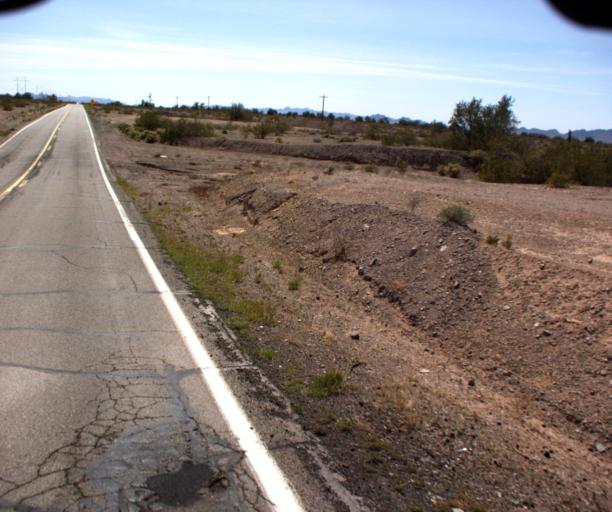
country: US
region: Arizona
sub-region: La Paz County
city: Quartzsite
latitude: 33.4993
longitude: -114.2171
